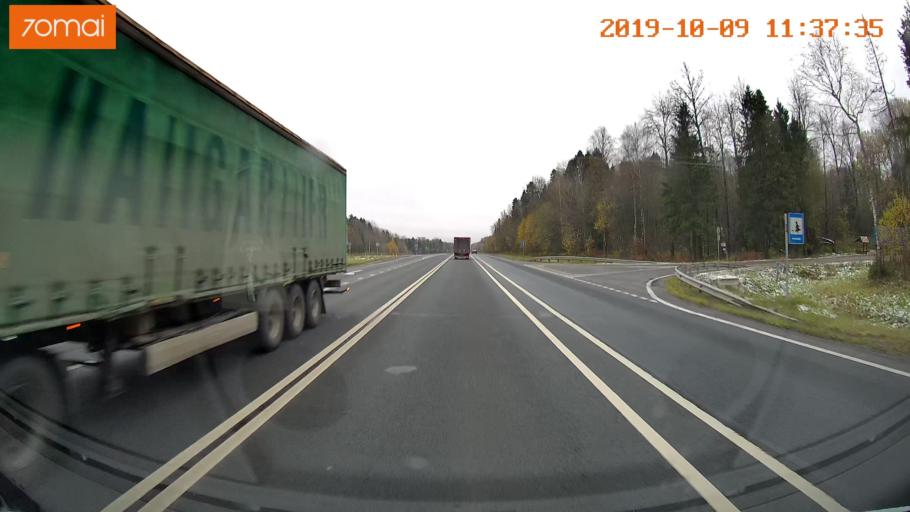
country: RU
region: Vologda
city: Gryazovets
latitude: 58.9778
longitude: 40.1477
